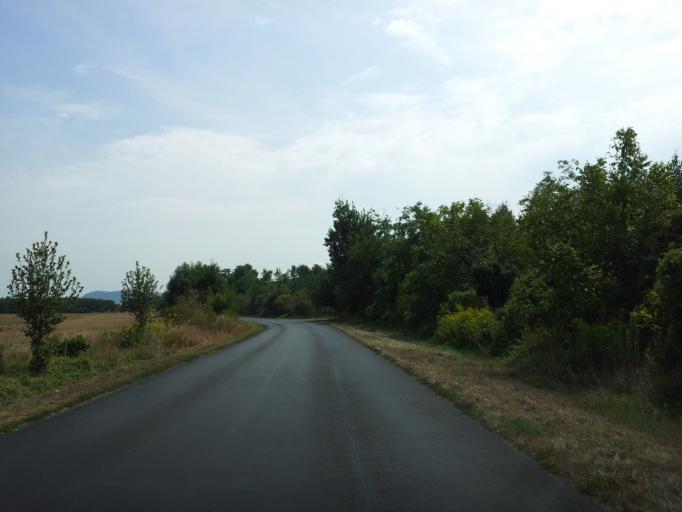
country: HU
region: Veszprem
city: Tapolca
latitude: 46.8656
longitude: 17.4509
